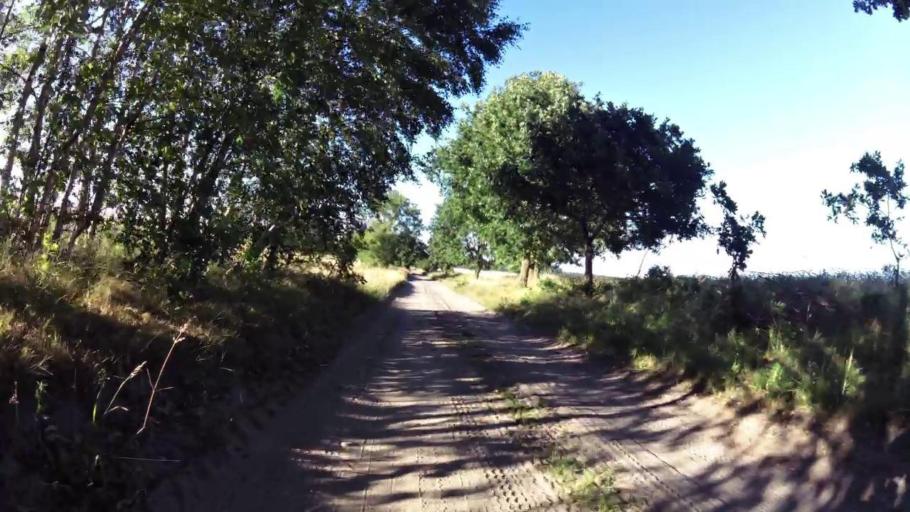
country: PL
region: West Pomeranian Voivodeship
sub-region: Powiat swidwinski
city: Swidwin
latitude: 53.7042
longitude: 15.8257
